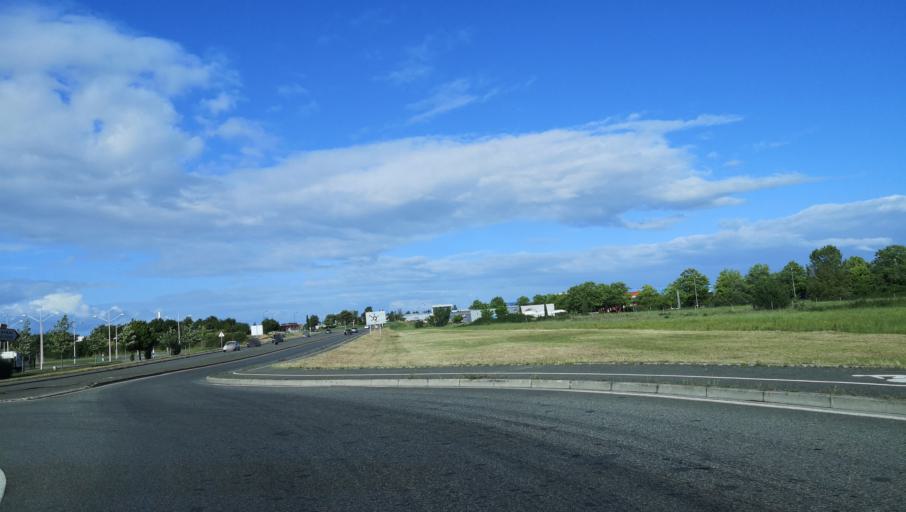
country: FR
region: Midi-Pyrenees
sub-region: Departement de la Haute-Garonne
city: Beauzelle
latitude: 43.6443
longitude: 1.3624
